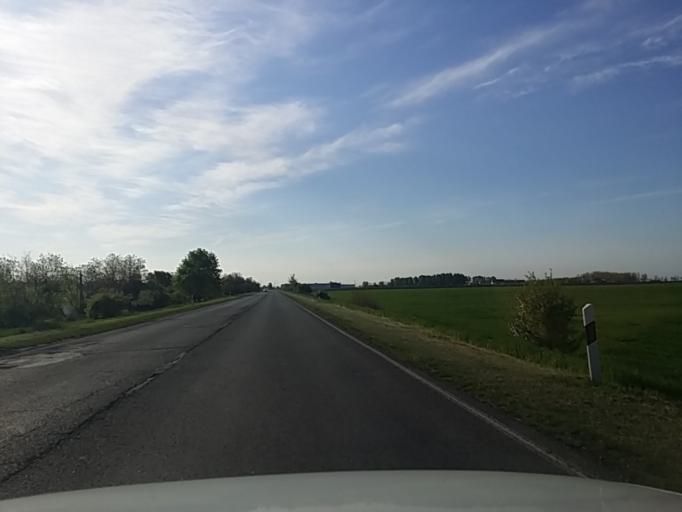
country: HU
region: Jasz-Nagykun-Szolnok
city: Torokszentmiklos
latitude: 47.1783
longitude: 20.3700
